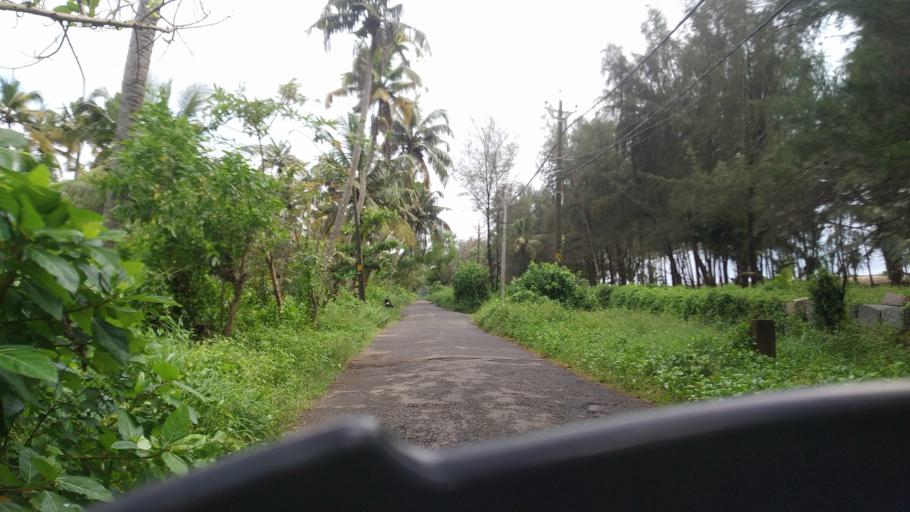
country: IN
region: Kerala
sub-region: Thrissur District
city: Kodungallur
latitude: 10.1212
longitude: 76.1848
